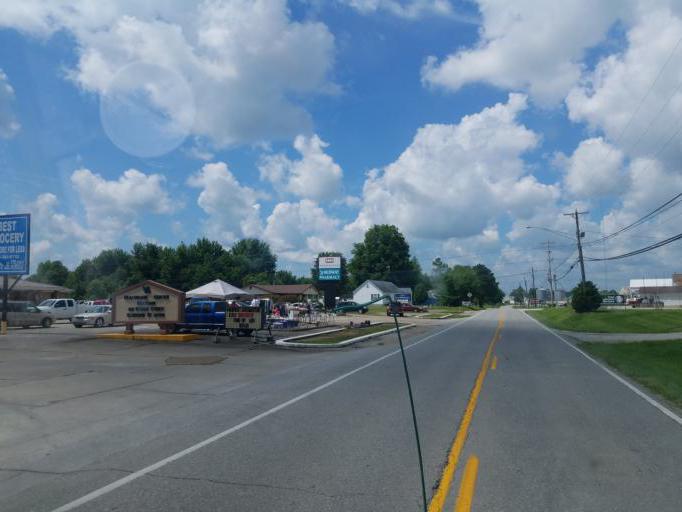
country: US
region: Kentucky
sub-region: Grayson County
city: Leitchfield
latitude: 37.4941
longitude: -86.2388
